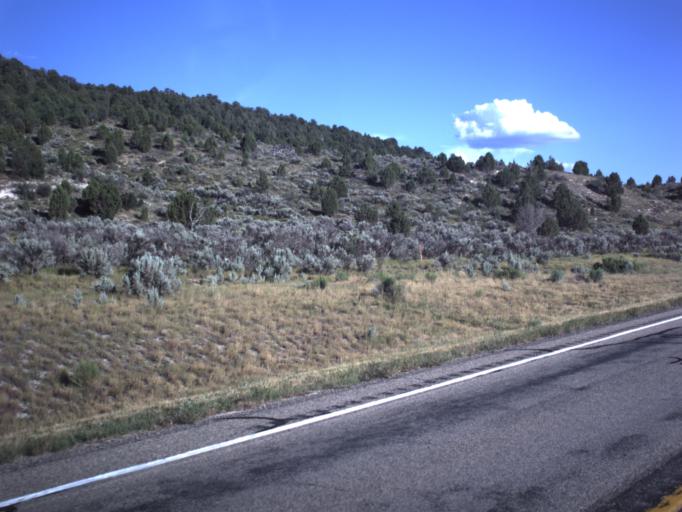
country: US
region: Utah
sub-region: Sanpete County
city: Fairview
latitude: 39.7367
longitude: -111.4771
